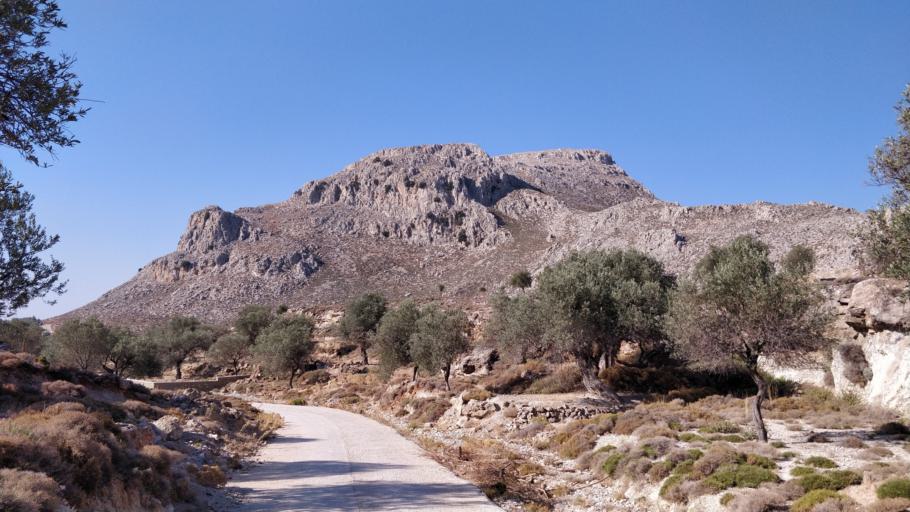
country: GR
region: South Aegean
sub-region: Nomos Dodekanisou
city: Archangelos
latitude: 36.2103
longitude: 28.1228
